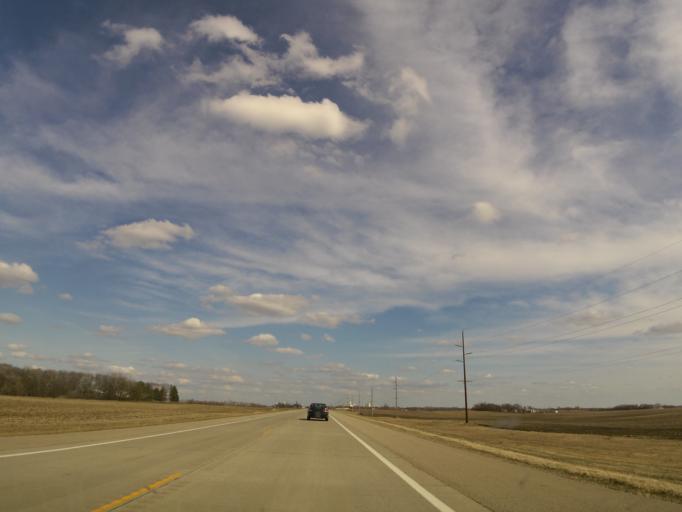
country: US
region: Minnesota
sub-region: Lac qui Parle County
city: Dawson
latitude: 44.9357
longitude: -96.1018
